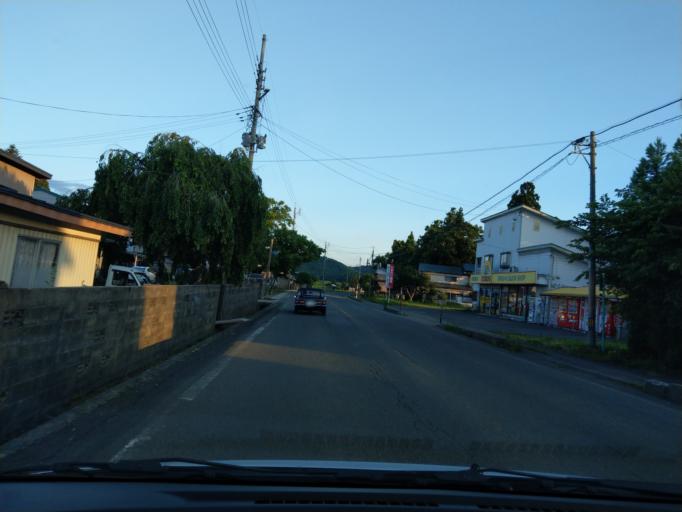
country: JP
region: Akita
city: Kakunodatemachi
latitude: 39.6211
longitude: 140.5721
